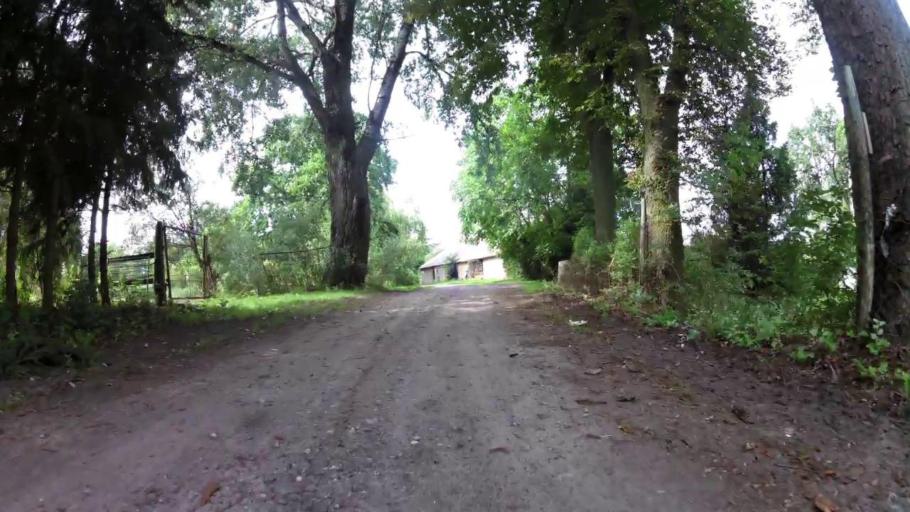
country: PL
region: West Pomeranian Voivodeship
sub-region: Powiat lobeski
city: Wegorzyno
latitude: 53.5355
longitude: 15.6122
